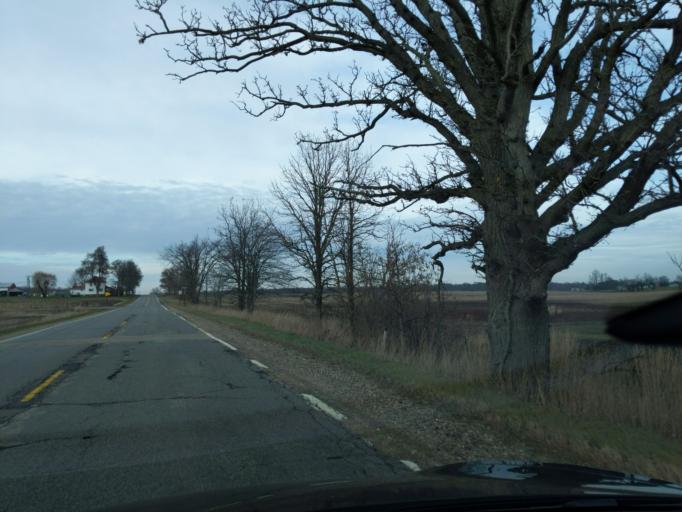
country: US
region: Michigan
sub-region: Ingham County
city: Williamston
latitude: 42.6532
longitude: -84.3637
